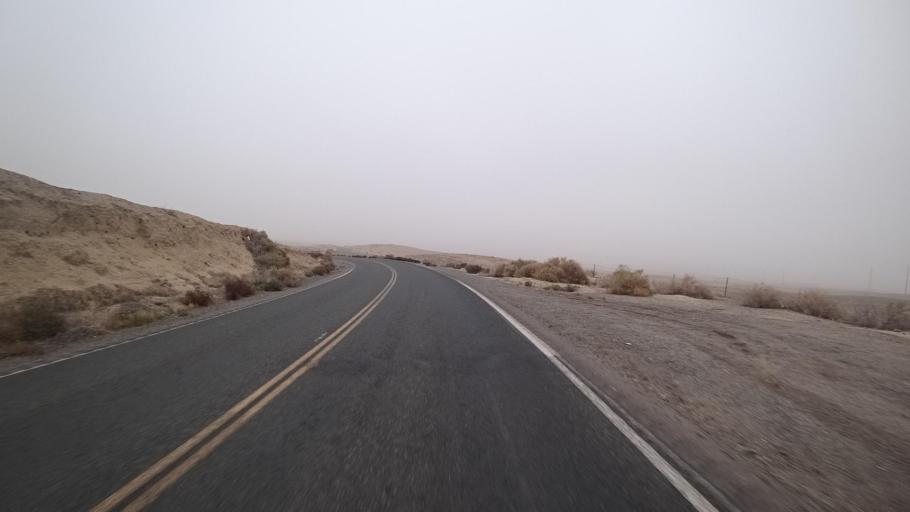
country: US
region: California
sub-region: Kern County
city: Buttonwillow
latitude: 35.3188
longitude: -119.4642
